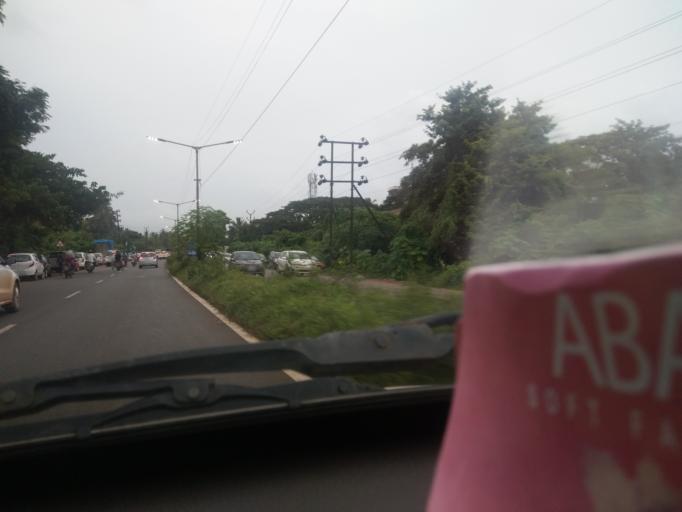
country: IN
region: Goa
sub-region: South Goa
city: Davorlim
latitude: 15.2780
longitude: 73.9808
